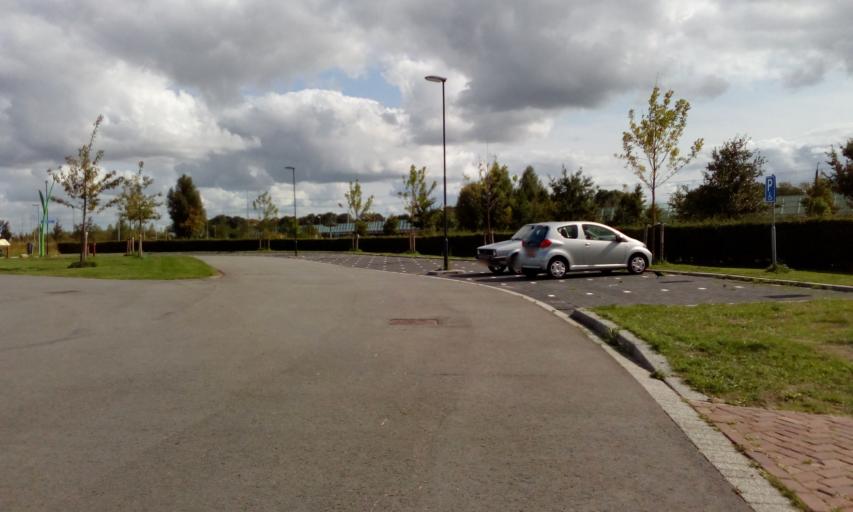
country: NL
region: South Holland
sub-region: Gemeente Rijnwoude
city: Benthuizen
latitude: 52.0603
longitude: 4.5526
